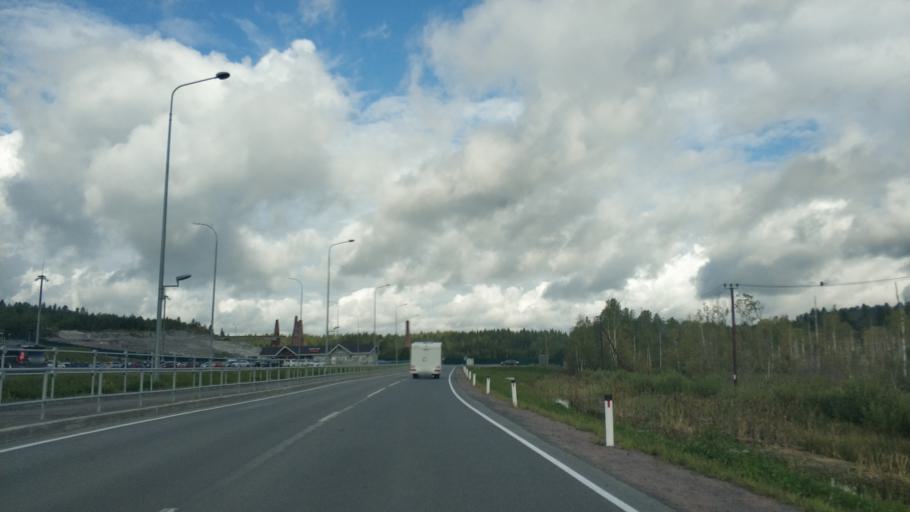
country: RU
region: Republic of Karelia
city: Ruskeala
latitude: 61.9483
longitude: 30.5874
